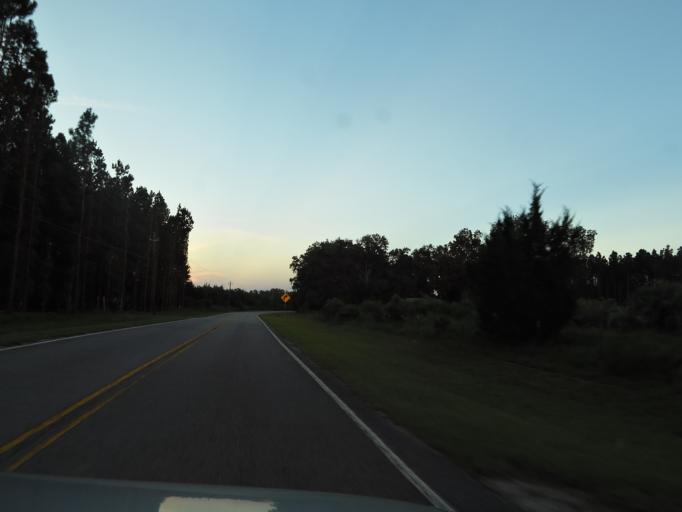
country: US
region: Georgia
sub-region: Camden County
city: Kingsland
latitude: 30.7736
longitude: -81.7002
